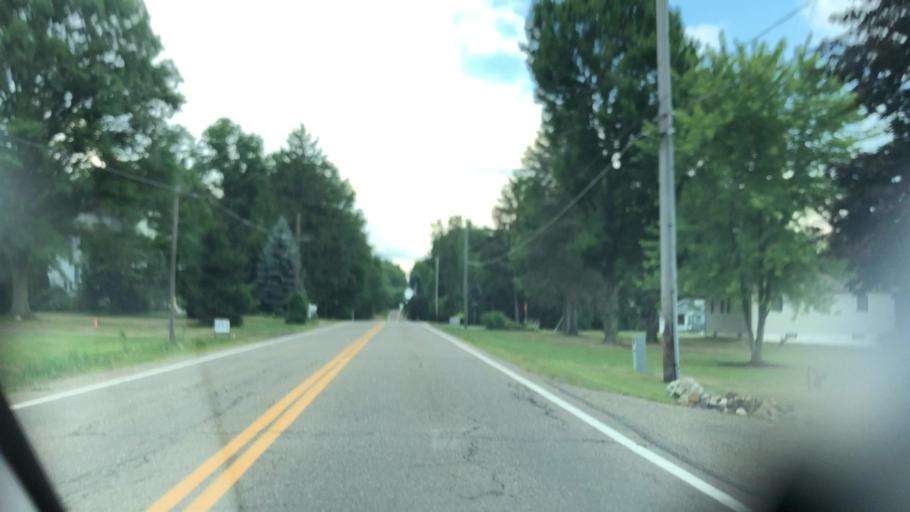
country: US
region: Ohio
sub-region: Summit County
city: Barberton
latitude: 41.0088
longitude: -81.5683
